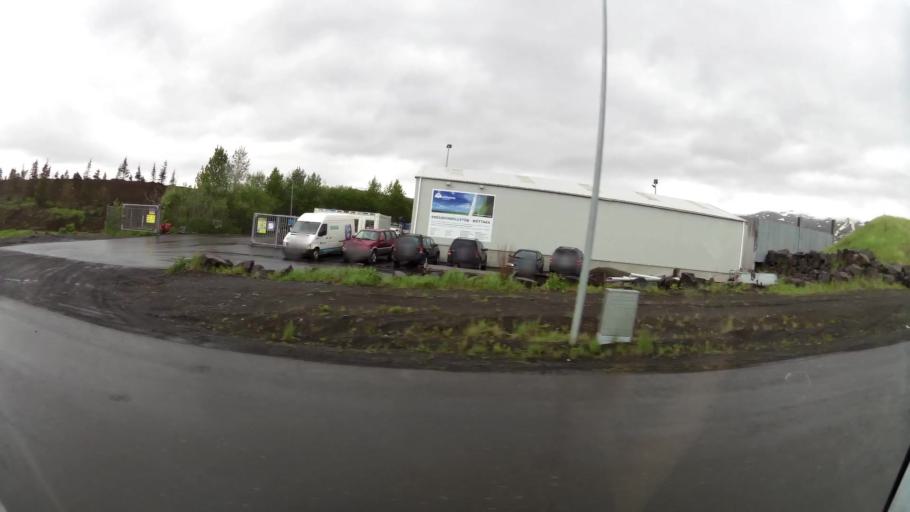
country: IS
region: Northeast
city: Akureyri
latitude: 65.7049
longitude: -18.1224
